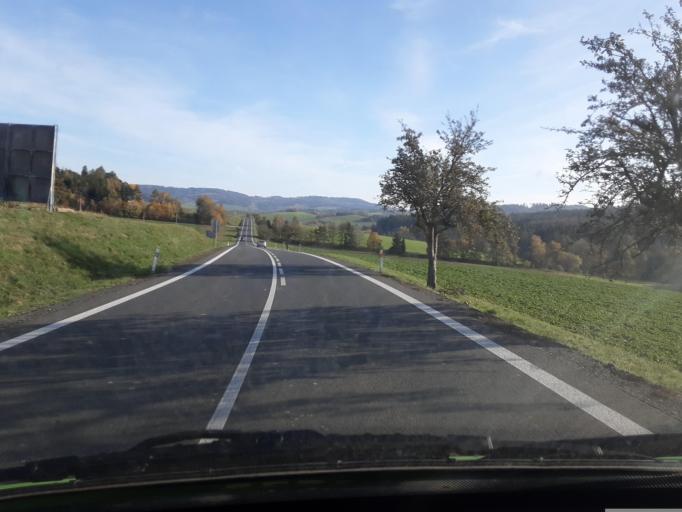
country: CZ
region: Plzensky
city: Klatovy
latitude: 49.3707
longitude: 13.3198
